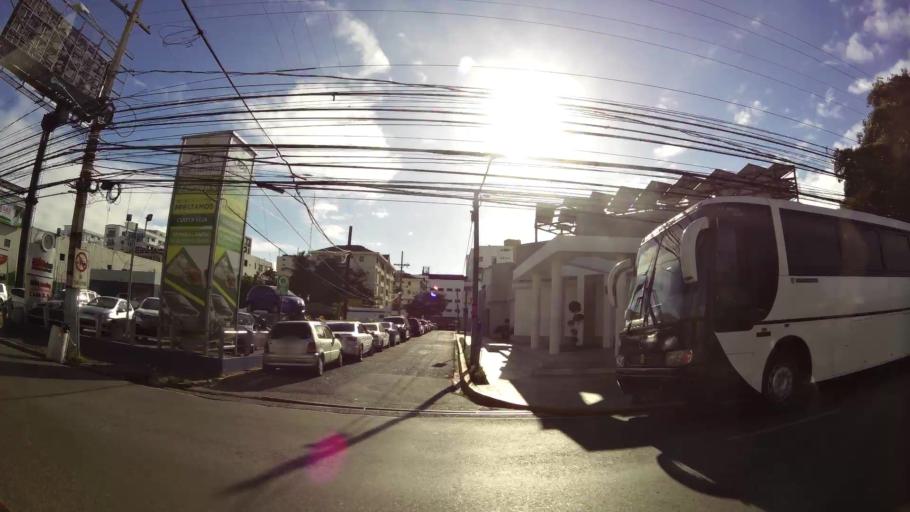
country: DO
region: Nacional
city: La Julia
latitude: 18.4771
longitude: -69.9313
